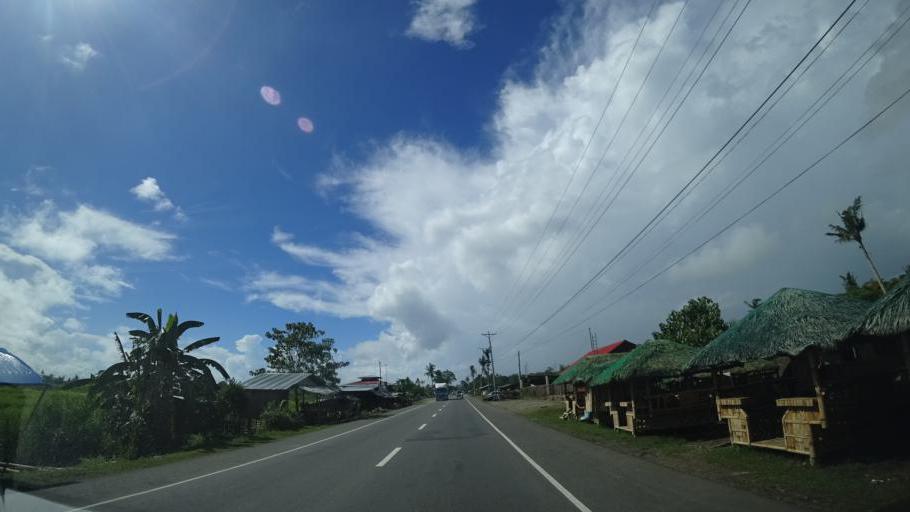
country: PH
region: Eastern Visayas
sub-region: Province of Leyte
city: Tanauan
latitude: 11.1187
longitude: 125.0169
